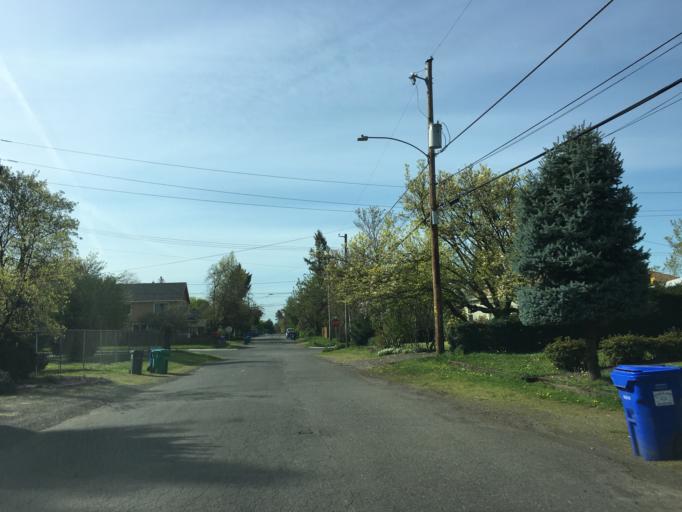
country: US
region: Oregon
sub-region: Multnomah County
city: Lents
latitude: 45.5233
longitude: -122.5668
